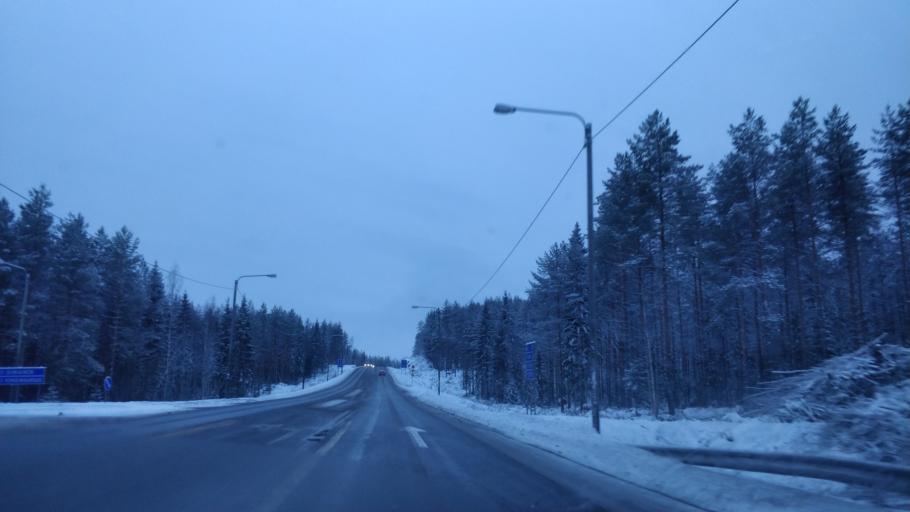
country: FI
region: Central Finland
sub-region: AEaenekoski
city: AEaenekoski
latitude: 62.8037
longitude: 25.8075
